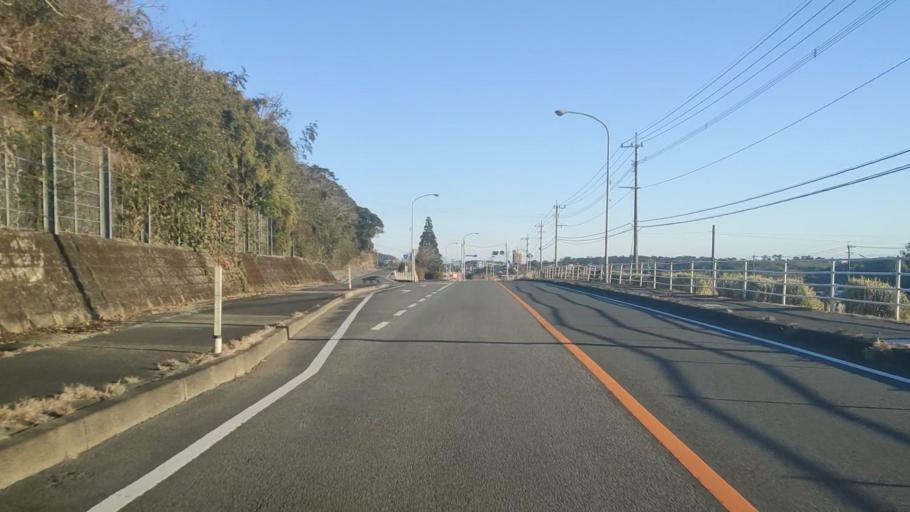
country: JP
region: Miyazaki
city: Takanabe
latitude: 32.1126
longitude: 131.5275
